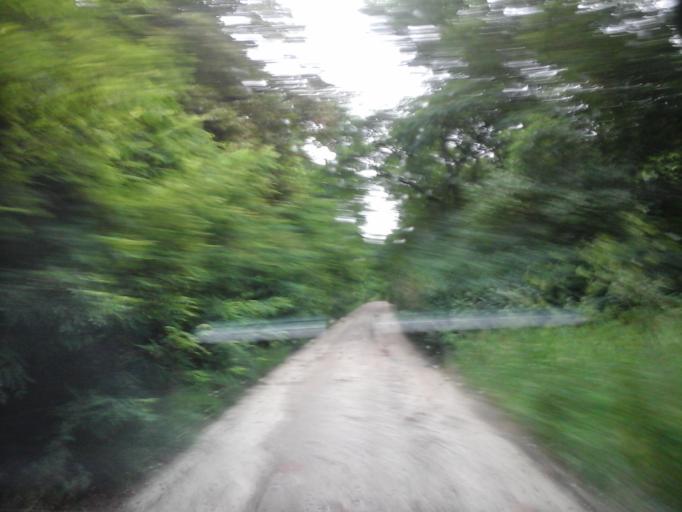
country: PL
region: West Pomeranian Voivodeship
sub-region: Powiat choszczenski
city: Bierzwnik
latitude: 53.1038
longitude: 15.6300
